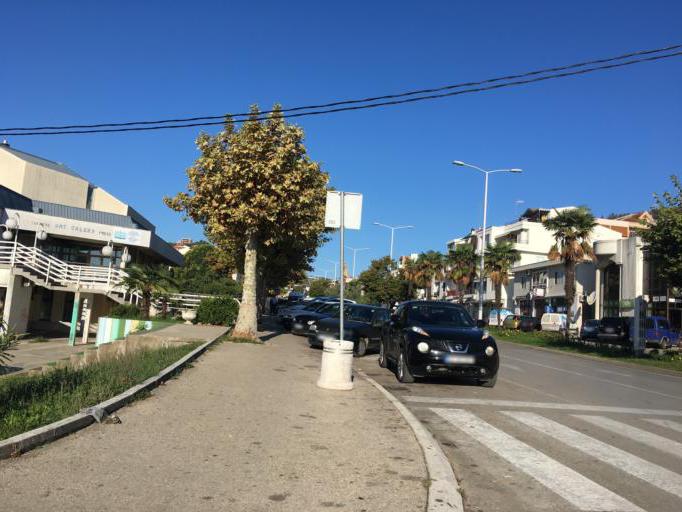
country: ME
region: Ulcinj
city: Ulcinj
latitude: 41.9298
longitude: 19.2151
